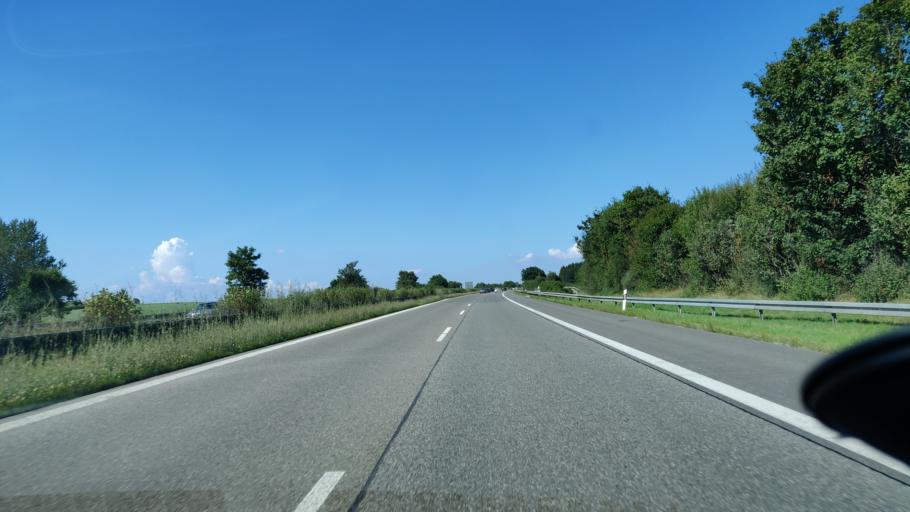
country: DE
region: Baden-Wuerttemberg
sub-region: Freiburg Region
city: Tuningen
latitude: 48.0061
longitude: 8.6053
